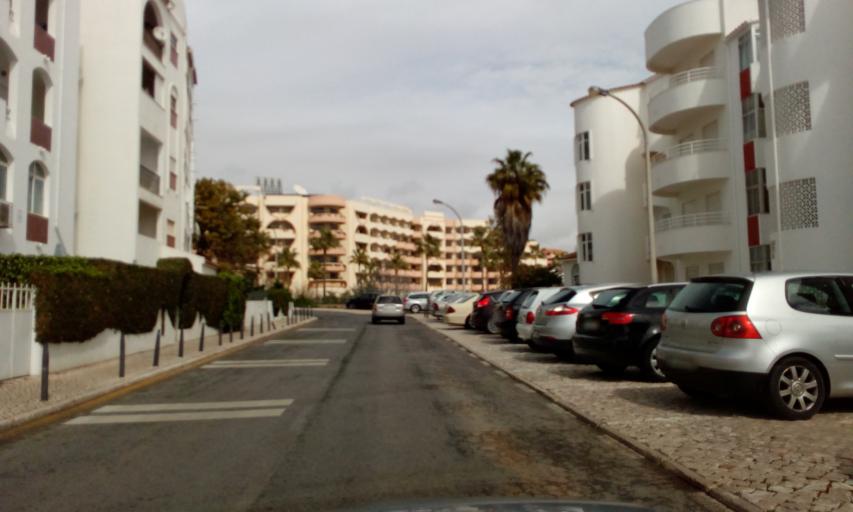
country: PT
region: Faro
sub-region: Albufeira
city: Albufeira
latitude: 37.0889
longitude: -8.2439
